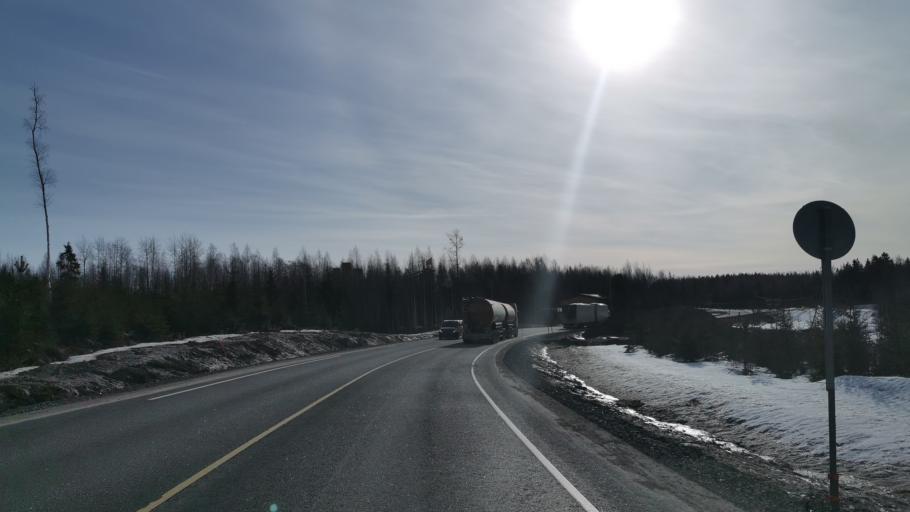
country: FI
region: Kymenlaakso
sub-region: Kouvola
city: Kouvola
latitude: 60.8694
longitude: 26.5487
